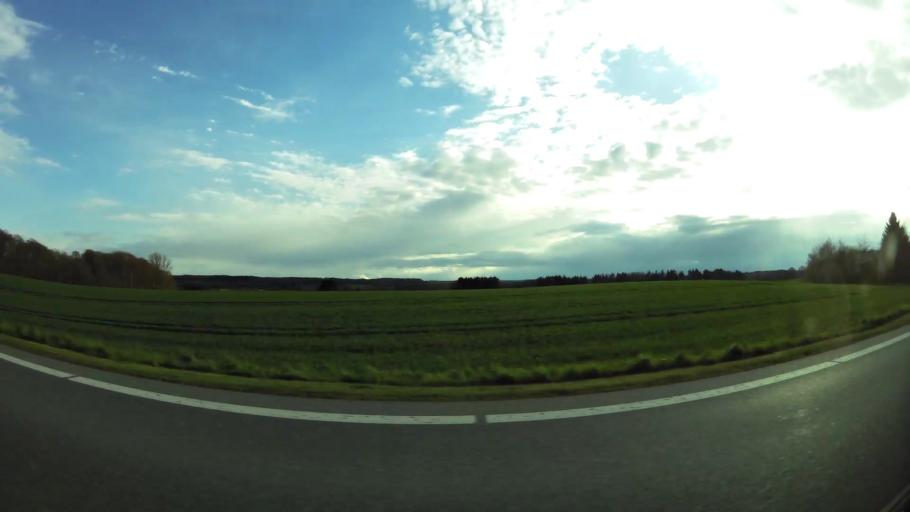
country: DK
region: Central Jutland
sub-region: Syddjurs Kommune
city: Hornslet
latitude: 56.3627
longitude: 10.3303
